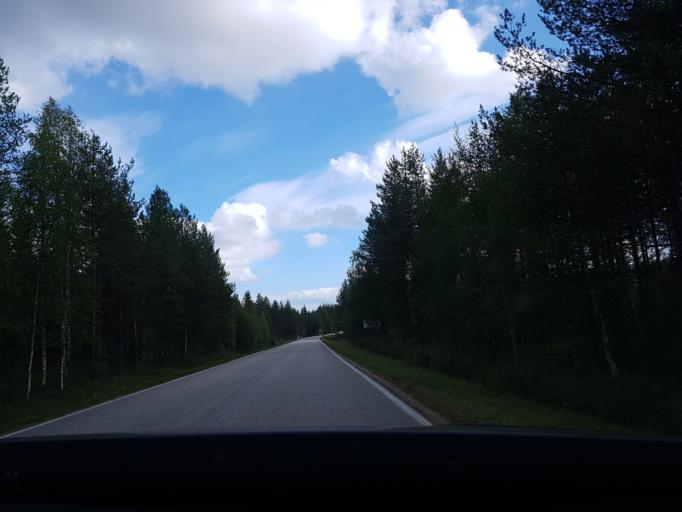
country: FI
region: Kainuu
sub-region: Kehys-Kainuu
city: Kuhmo
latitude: 64.6280
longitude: 29.6939
